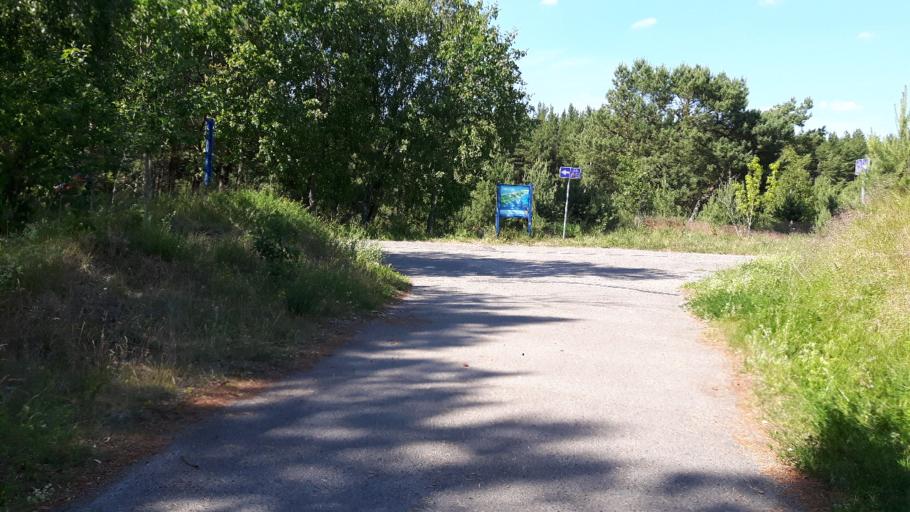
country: LT
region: Klaipedos apskritis
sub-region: Klaipeda
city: Klaipeda
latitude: 55.6939
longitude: 21.1032
